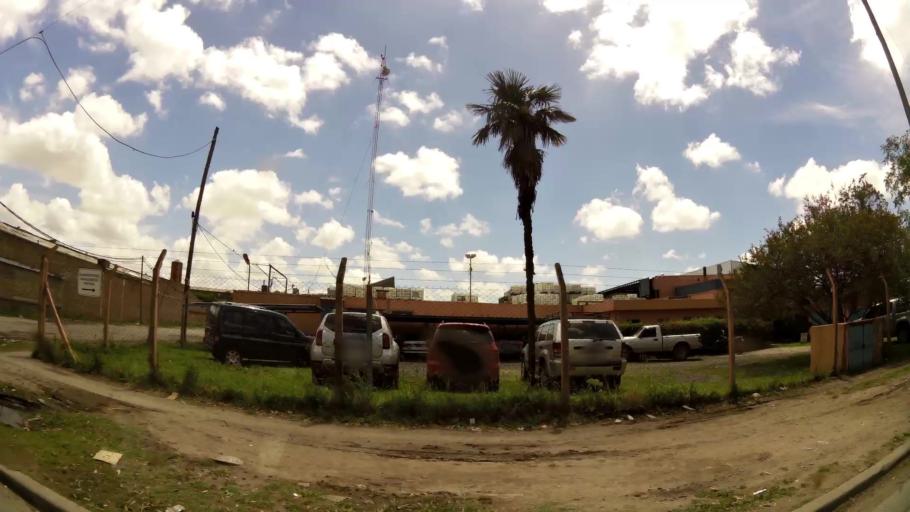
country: AR
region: Buenos Aires
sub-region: Partido de Quilmes
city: Quilmes
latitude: -34.8117
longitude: -58.2311
